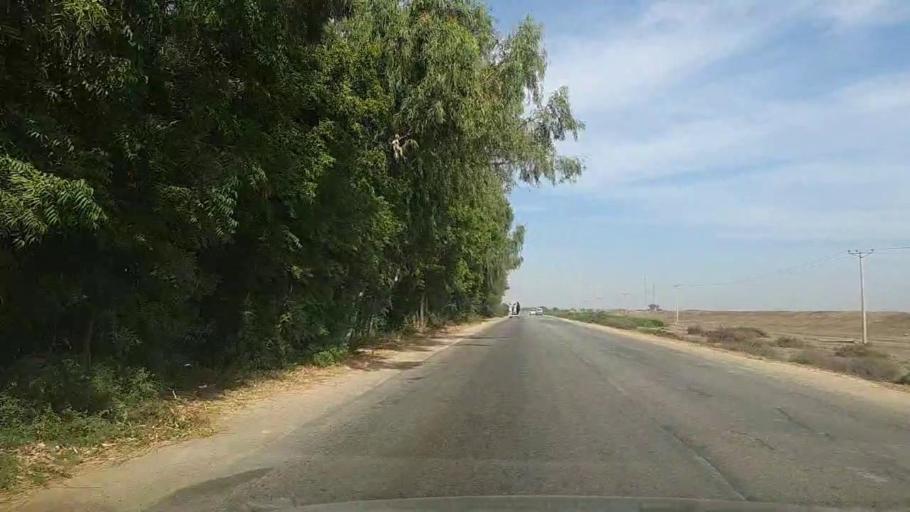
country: PK
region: Sindh
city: Daro Mehar
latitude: 24.9589
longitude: 68.1165
